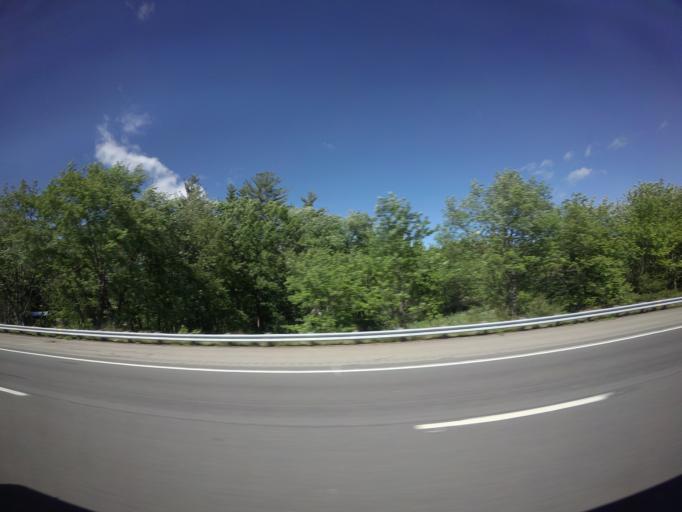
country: US
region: New Hampshire
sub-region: Hillsborough County
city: Manchester
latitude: 42.9525
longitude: -71.4007
